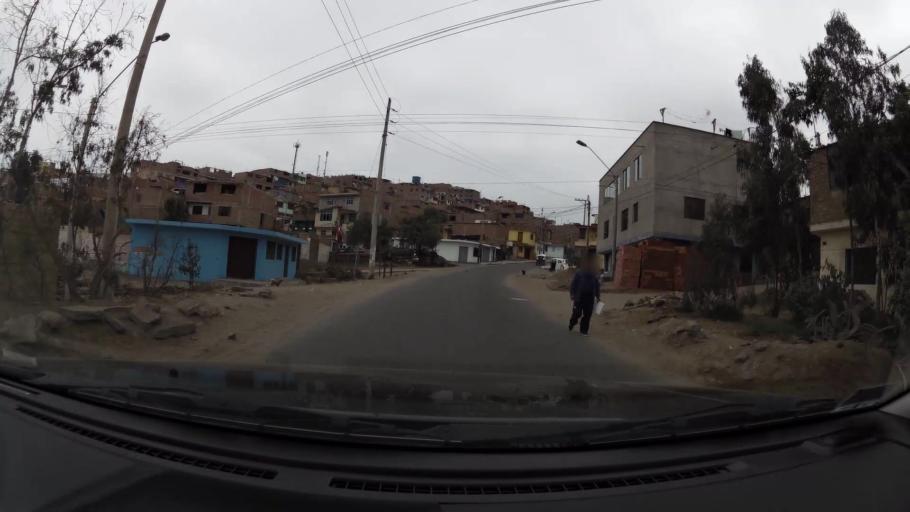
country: PE
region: Lima
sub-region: Lima
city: Surco
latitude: -12.1915
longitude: -76.9904
